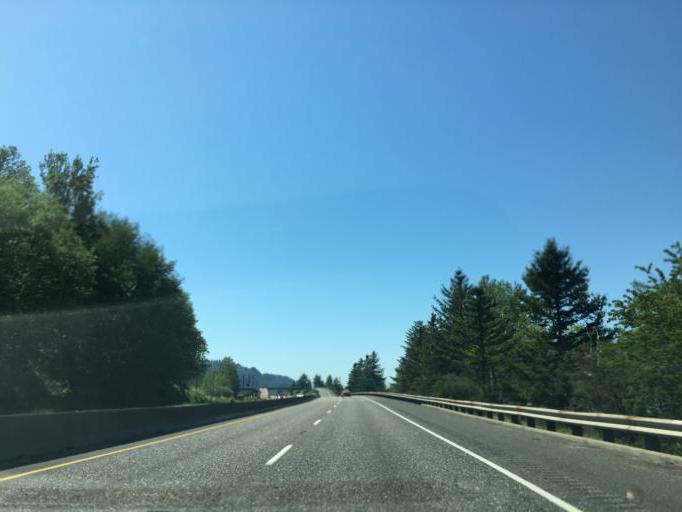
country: US
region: Washington
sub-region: Clark County
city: Washougal
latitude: 45.5418
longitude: -122.2879
